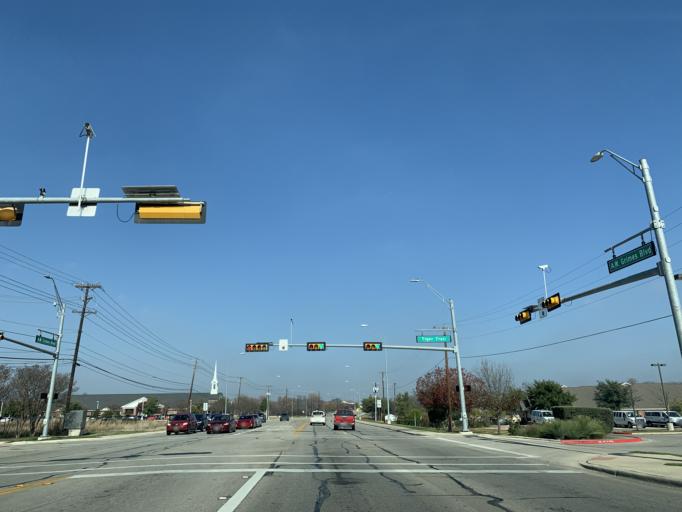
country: US
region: Texas
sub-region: Williamson County
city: Round Rock
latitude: 30.5318
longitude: -97.6521
